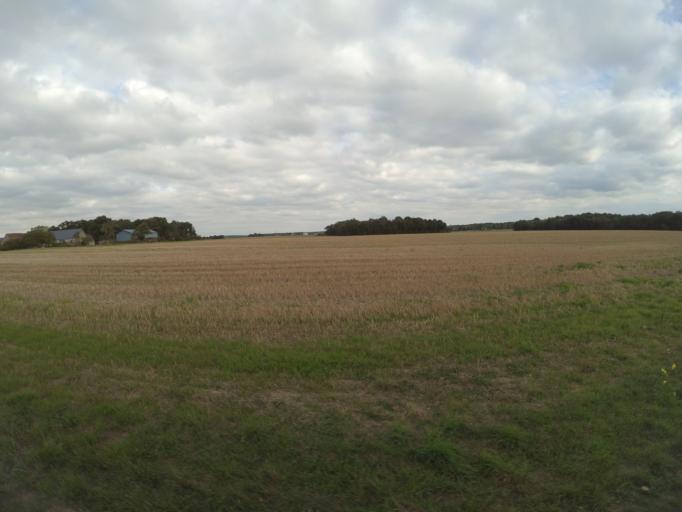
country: FR
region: Centre
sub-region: Departement d'Indre-et-Loire
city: Nazelles-Negron
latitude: 47.4758
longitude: 0.9430
